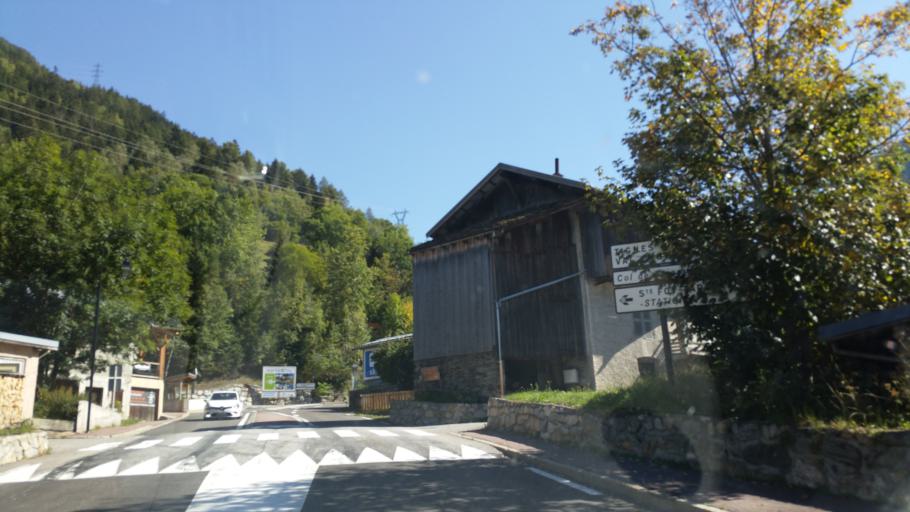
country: FR
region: Rhone-Alpes
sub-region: Departement de la Savoie
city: Tignes
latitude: 45.5734
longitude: 6.8854
